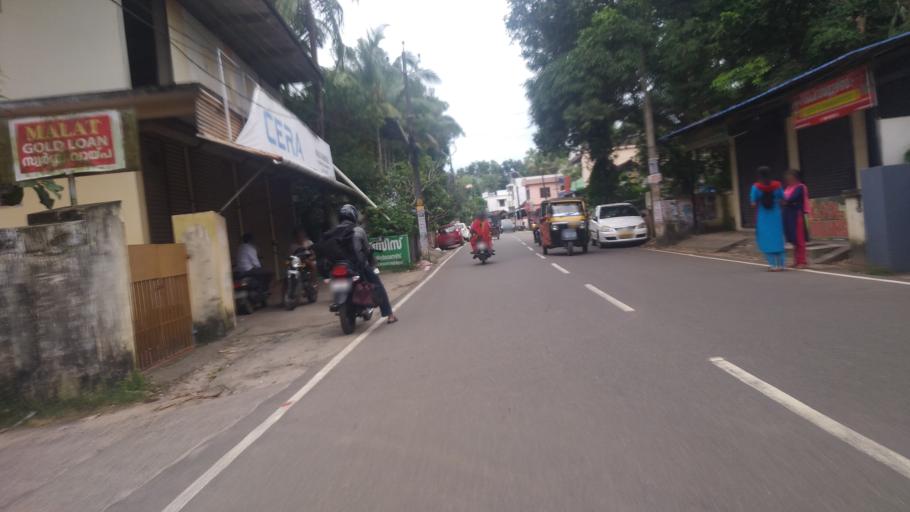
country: IN
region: Kerala
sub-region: Alappuzha
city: Arukutti
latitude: 9.8660
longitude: 76.2916
